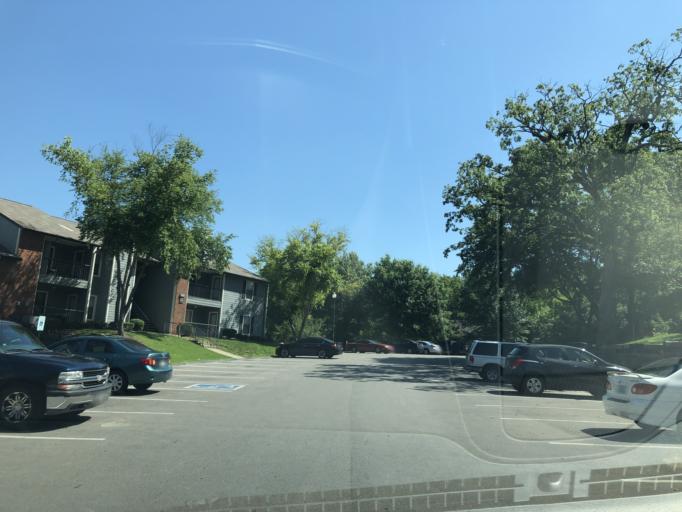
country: US
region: Tennessee
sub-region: Williamson County
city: Nolensville
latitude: 36.0387
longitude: -86.6701
